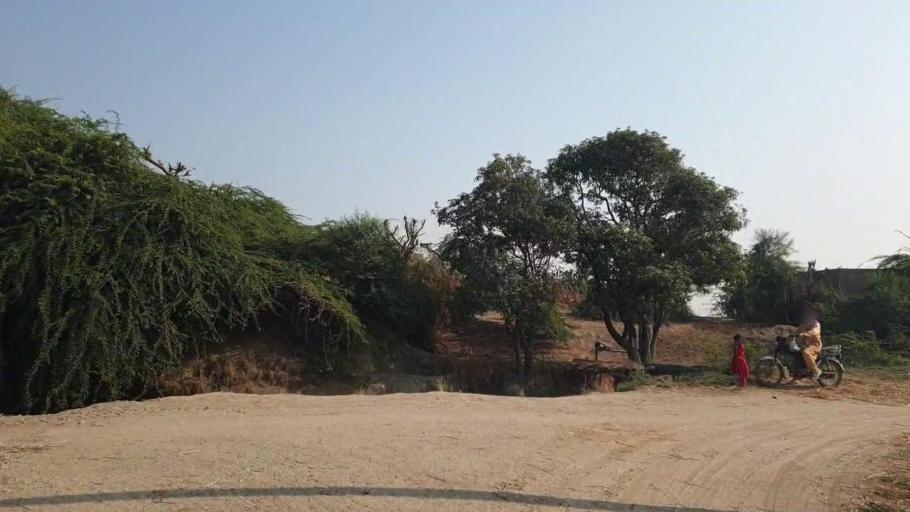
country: PK
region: Sindh
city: Matli
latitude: 25.0078
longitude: 68.6317
